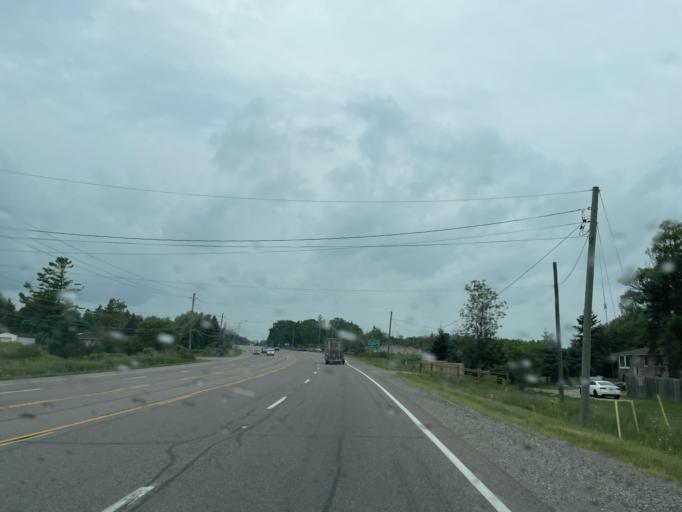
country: CA
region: Ontario
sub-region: Halton
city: Milton
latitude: 43.4179
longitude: -80.0627
